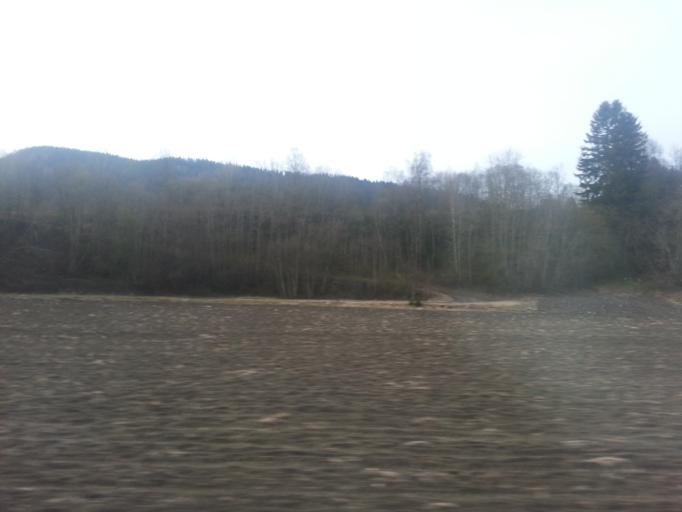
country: NO
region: Sor-Trondelag
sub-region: Melhus
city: Lundamo
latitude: 63.1627
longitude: 10.2951
